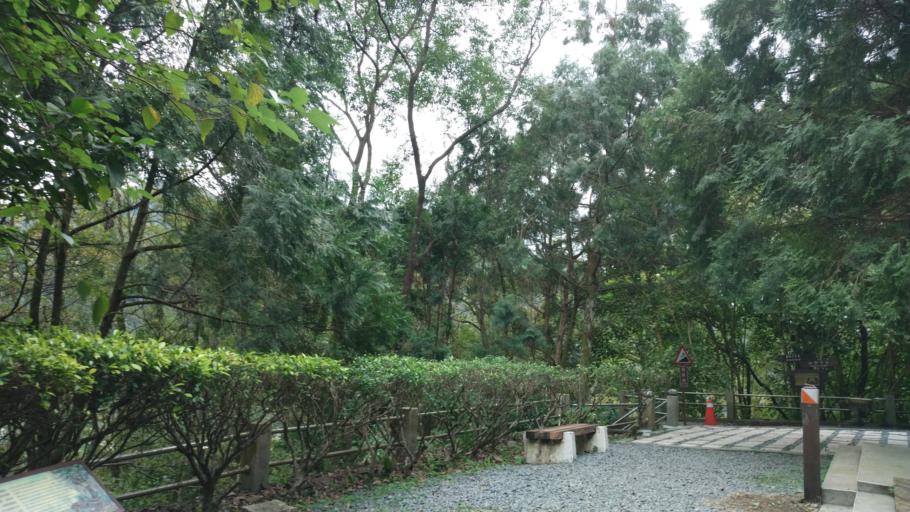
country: TW
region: Taiwan
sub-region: Hualien
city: Hualian
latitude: 23.9177
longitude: 121.5014
